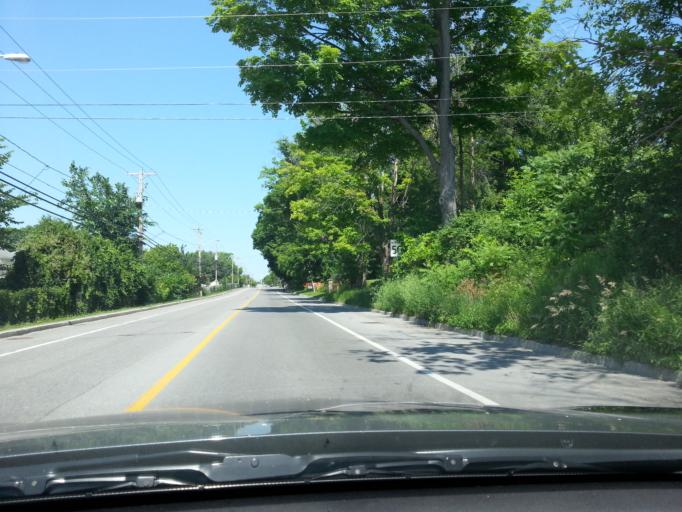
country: CA
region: Ontario
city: Bells Corners
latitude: 45.4033
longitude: -75.8576
